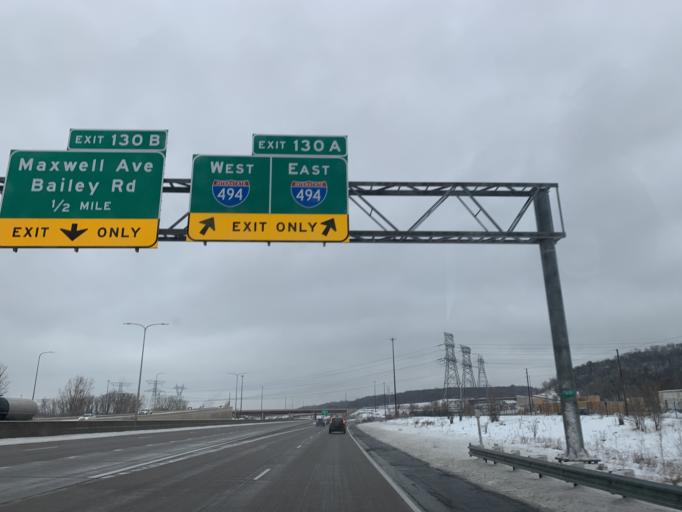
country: US
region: Minnesota
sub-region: Washington County
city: Newport
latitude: 44.8803
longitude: -93.0030
